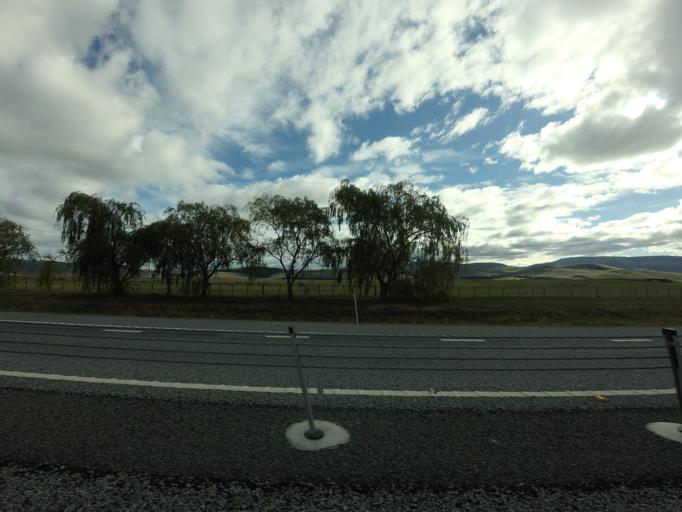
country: AU
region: Tasmania
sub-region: Brighton
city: Bridgewater
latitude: -42.4943
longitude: 147.1858
